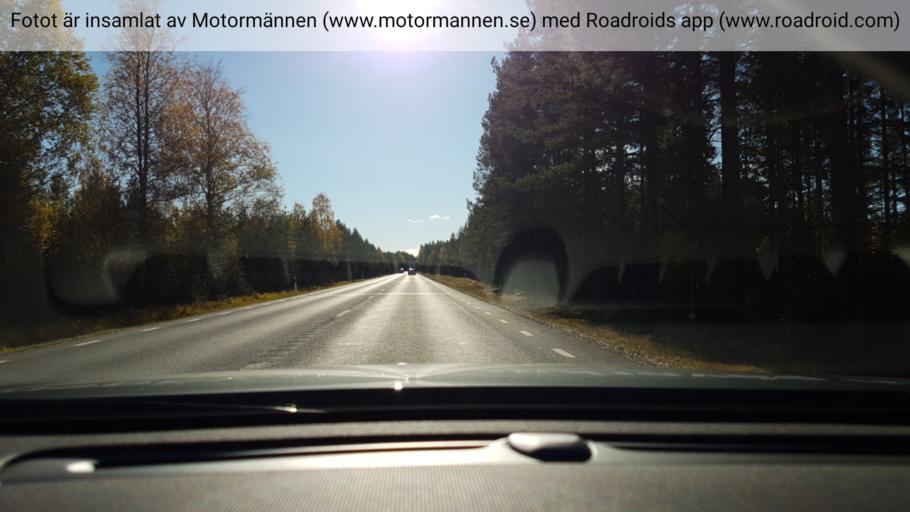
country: SE
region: Vaesterbotten
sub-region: Skelleftea Kommun
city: Burea
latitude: 64.5577
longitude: 21.2386
